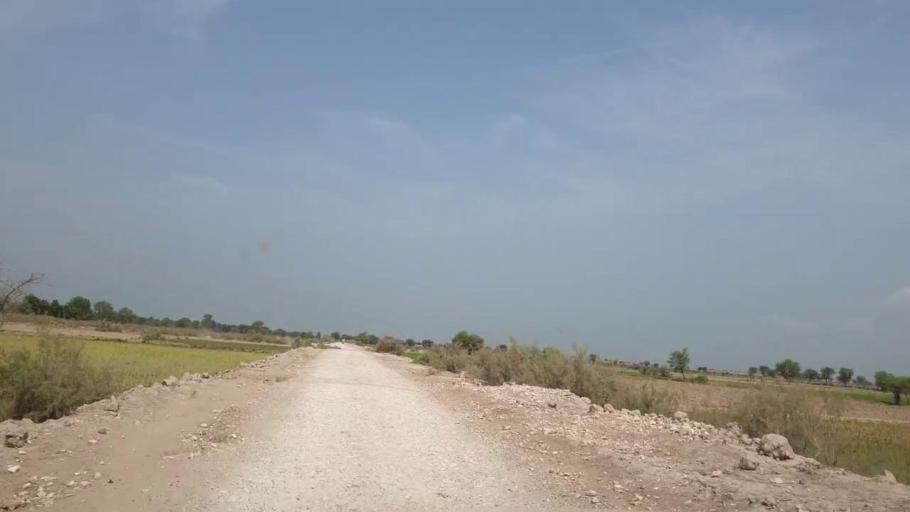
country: PK
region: Sindh
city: Dokri
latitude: 27.3996
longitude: 68.2540
